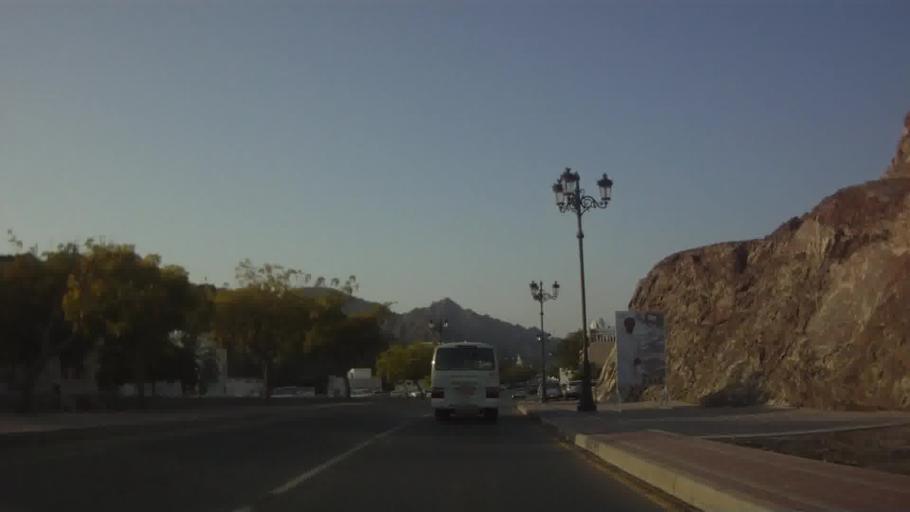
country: OM
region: Muhafazat Masqat
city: Muscat
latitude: 23.5911
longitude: 58.5988
